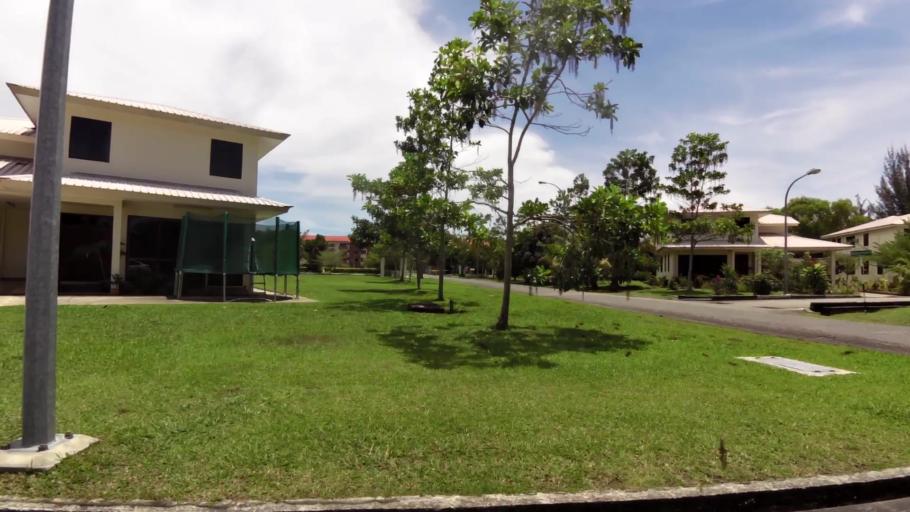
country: BN
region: Belait
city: Kuala Belait
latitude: 4.5899
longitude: 114.2511
